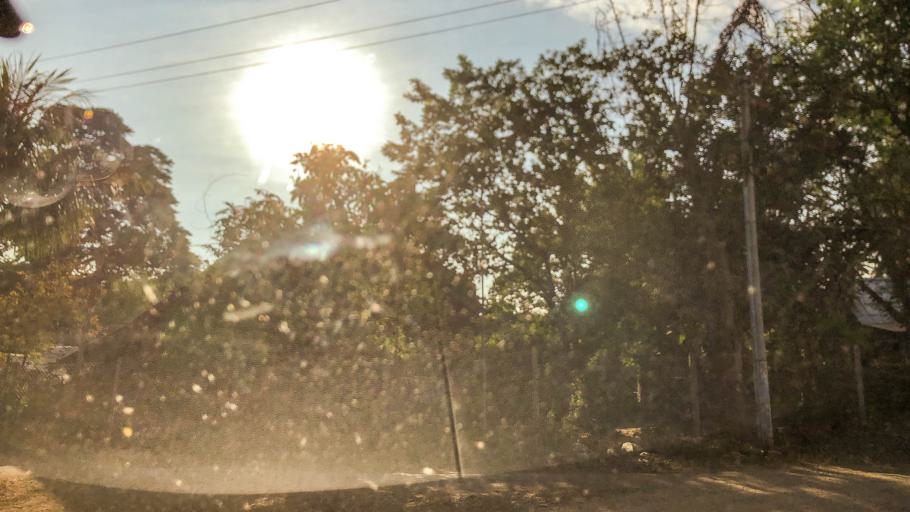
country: MM
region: Magway
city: Magway
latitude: 19.9724
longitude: 95.0404
